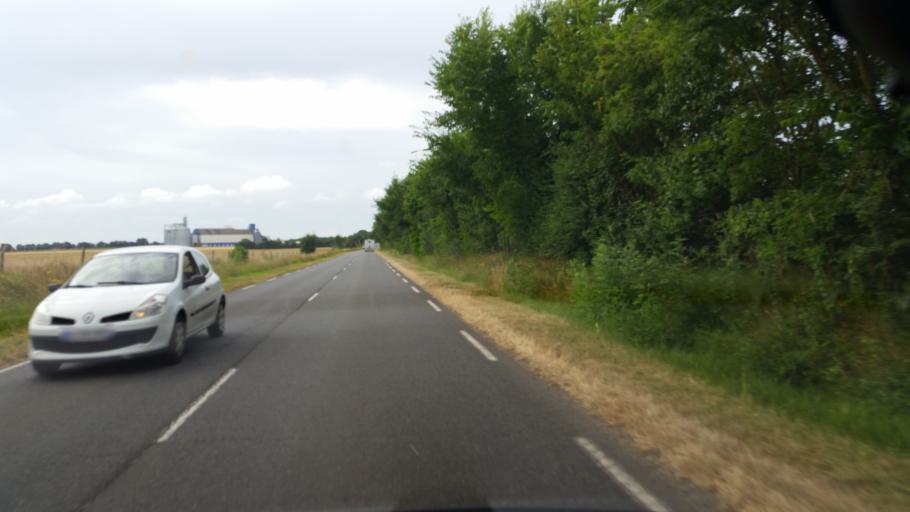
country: FR
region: Poitou-Charentes
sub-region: Departement de la Charente-Maritime
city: Courcon
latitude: 46.1680
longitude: -0.8367
